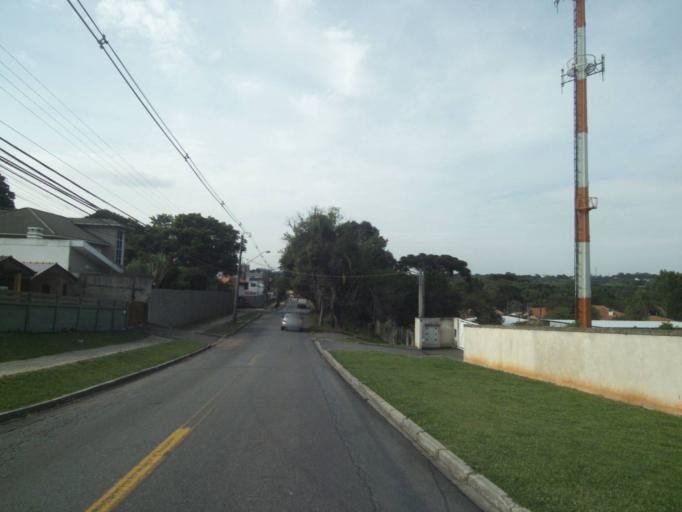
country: BR
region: Parana
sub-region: Curitiba
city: Curitiba
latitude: -25.4180
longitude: -49.3202
